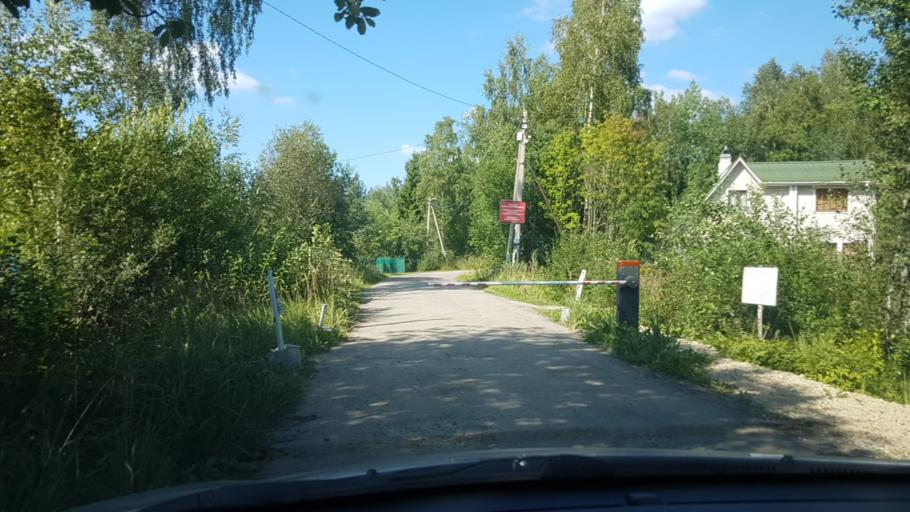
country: RU
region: Leningrad
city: Vyritsa
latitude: 59.4483
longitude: 30.2942
